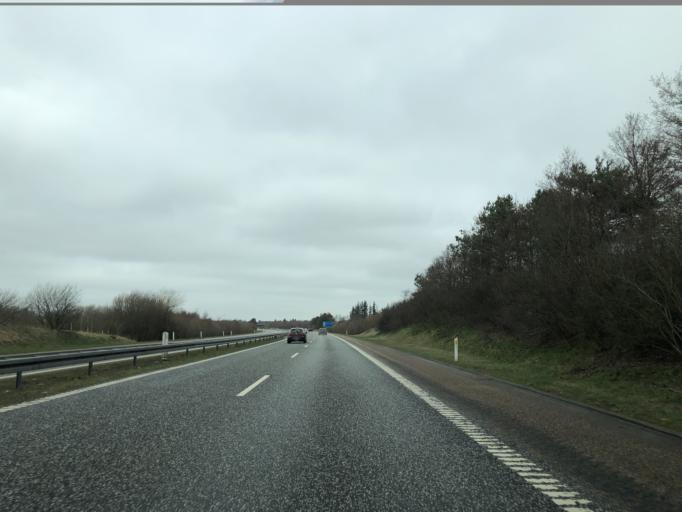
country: DK
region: North Denmark
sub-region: Frederikshavn Kommune
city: Saeby
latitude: 57.3056
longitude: 10.4434
